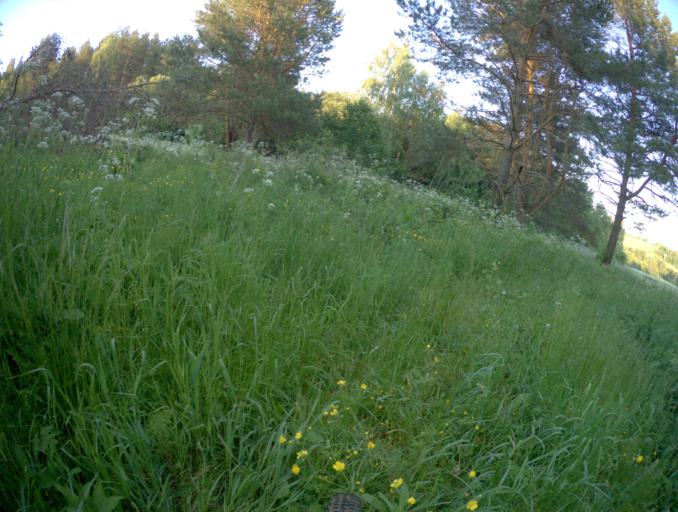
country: RU
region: Vladimir
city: Stavrovo
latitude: 56.3162
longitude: 39.9550
